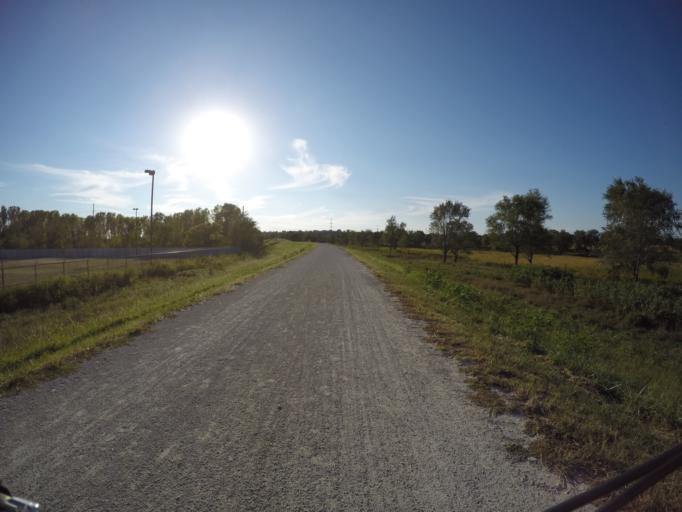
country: US
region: Kansas
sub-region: Riley County
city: Manhattan
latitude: 39.1969
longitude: -96.5447
